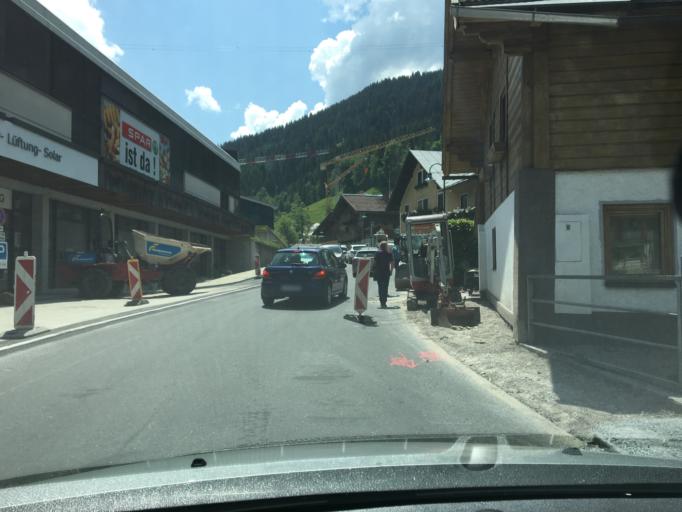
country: AT
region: Salzburg
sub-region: Politischer Bezirk Sankt Johann im Pongau
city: Wagrain
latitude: 47.3319
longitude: 13.2977
